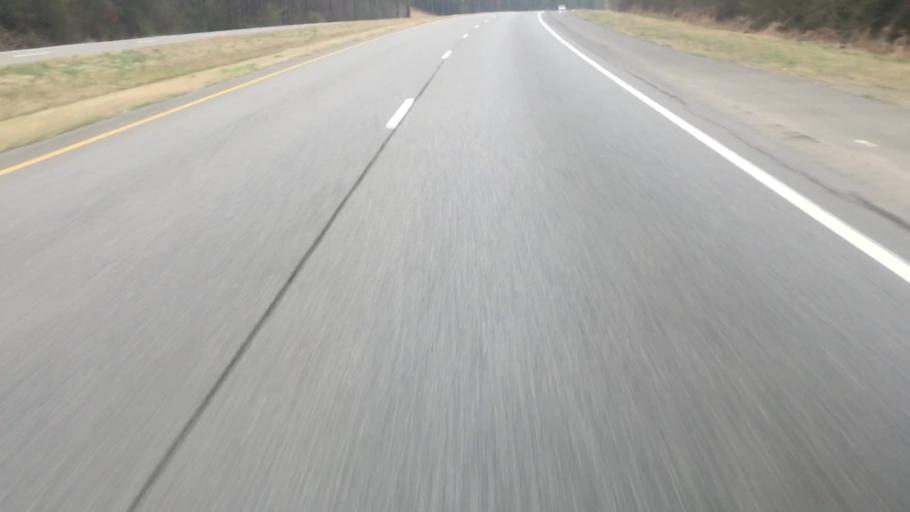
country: US
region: Alabama
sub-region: Jefferson County
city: Graysville
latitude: 33.6879
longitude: -86.9769
